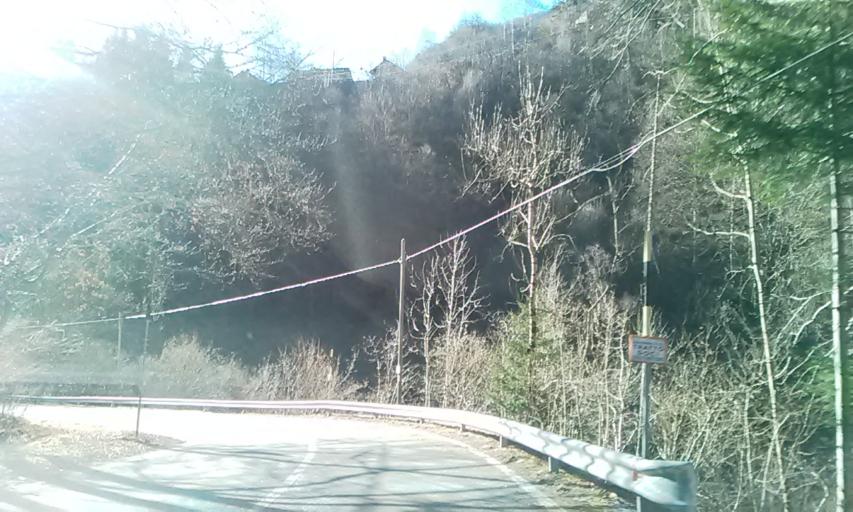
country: IT
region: Piedmont
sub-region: Provincia di Vercelli
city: Rimasco
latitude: 45.8693
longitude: 8.0677
